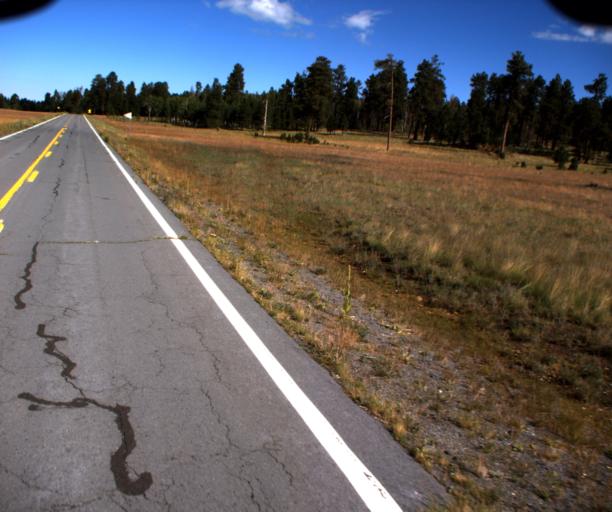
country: US
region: Arizona
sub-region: Apache County
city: Eagar
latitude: 33.9941
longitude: -109.3662
